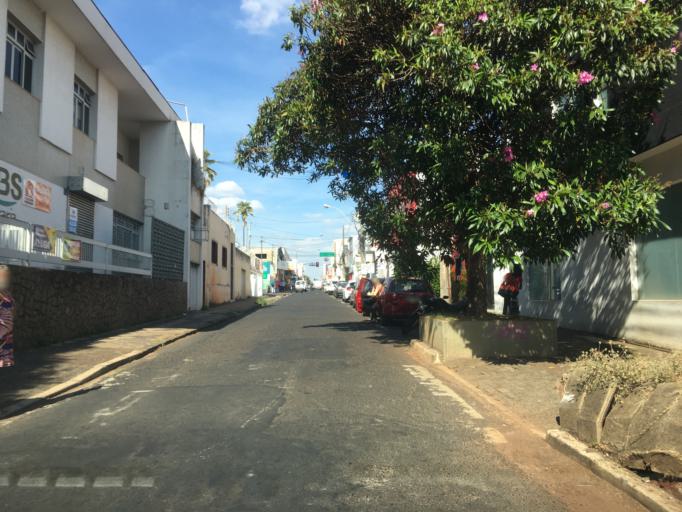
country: BR
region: Minas Gerais
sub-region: Uberlandia
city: Uberlandia
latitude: -18.9161
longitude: -48.2778
